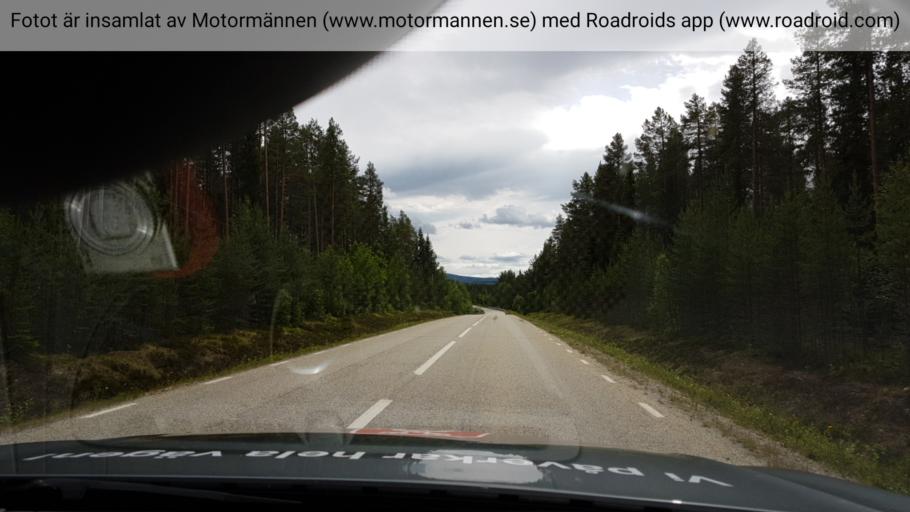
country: SE
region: Jaemtland
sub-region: Bergs Kommun
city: Hoverberg
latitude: 62.7261
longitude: 13.9092
